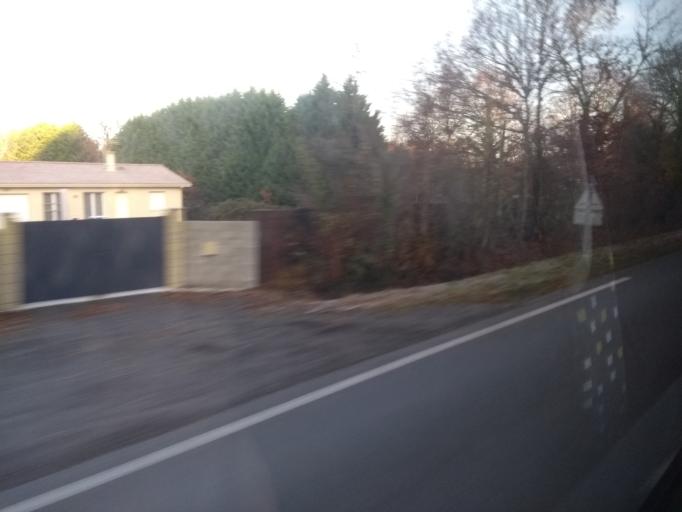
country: FR
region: Aquitaine
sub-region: Departement de la Gironde
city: Le Barp
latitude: 44.6132
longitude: -0.7657
